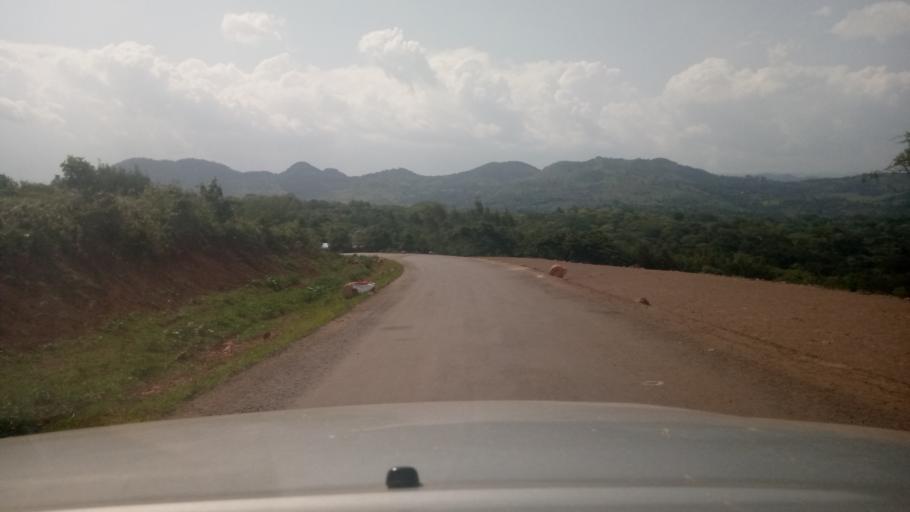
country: ET
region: Oromiya
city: Agaro
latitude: 7.9897
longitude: 36.5108
